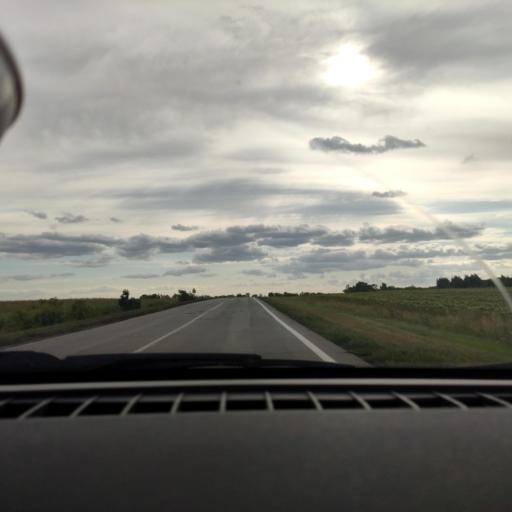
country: RU
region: Samara
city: Krasnyy Yar
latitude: 53.4332
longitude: 50.5580
